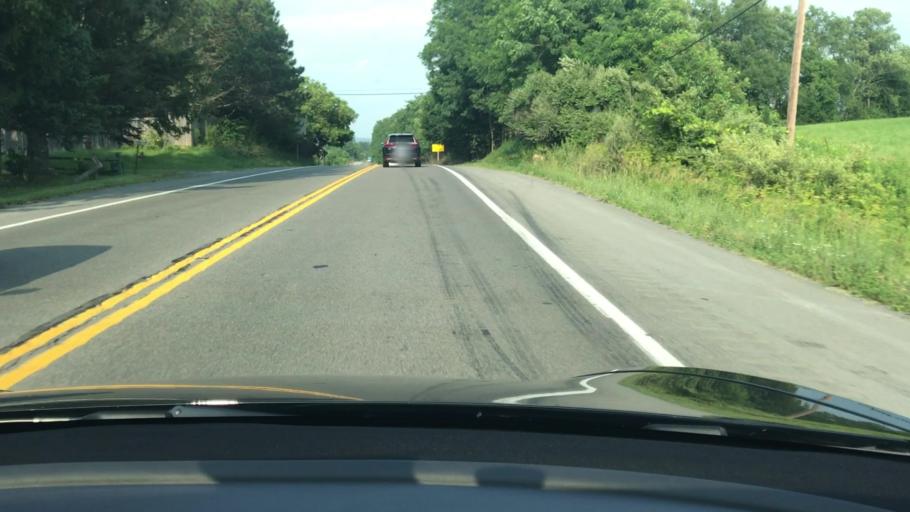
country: US
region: Pennsylvania
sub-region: Centre County
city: Centre Hall
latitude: 40.7952
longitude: -77.6787
